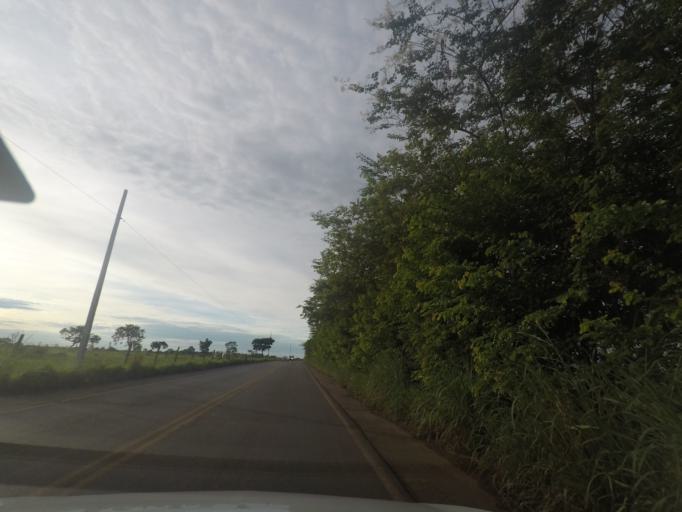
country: BR
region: Goias
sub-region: Trindade
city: Trindade
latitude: -16.7252
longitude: -49.4267
